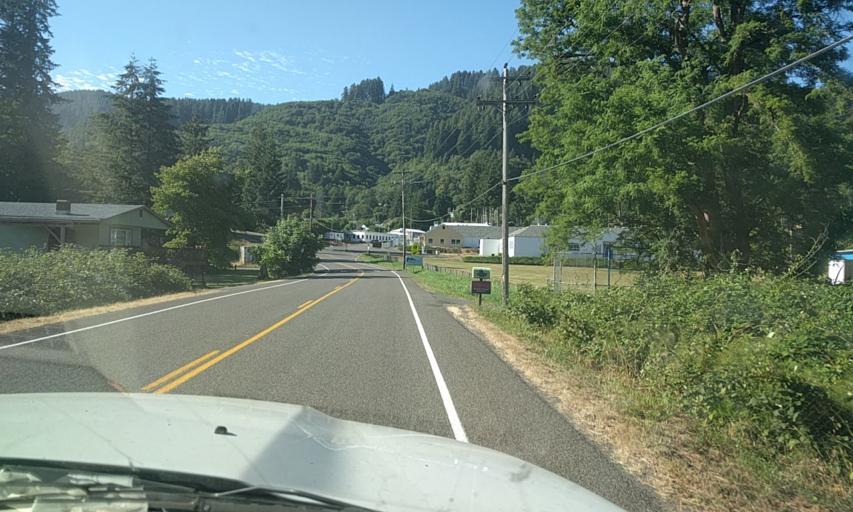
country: US
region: Oregon
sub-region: Lane County
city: Florence
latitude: 44.0337
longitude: -123.8550
